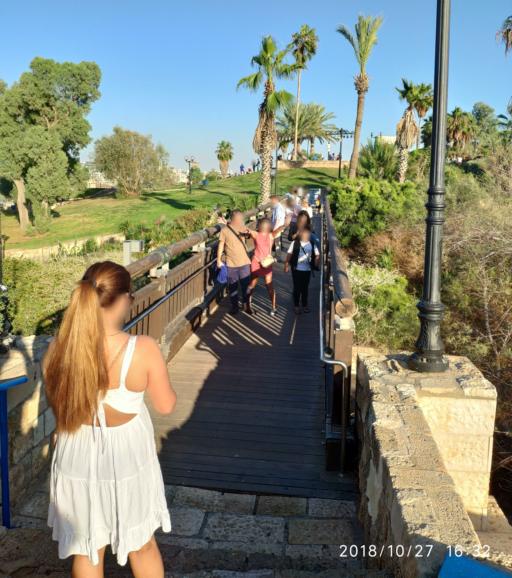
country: IL
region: Tel Aviv
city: Yafo
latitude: 32.0542
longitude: 34.7524
